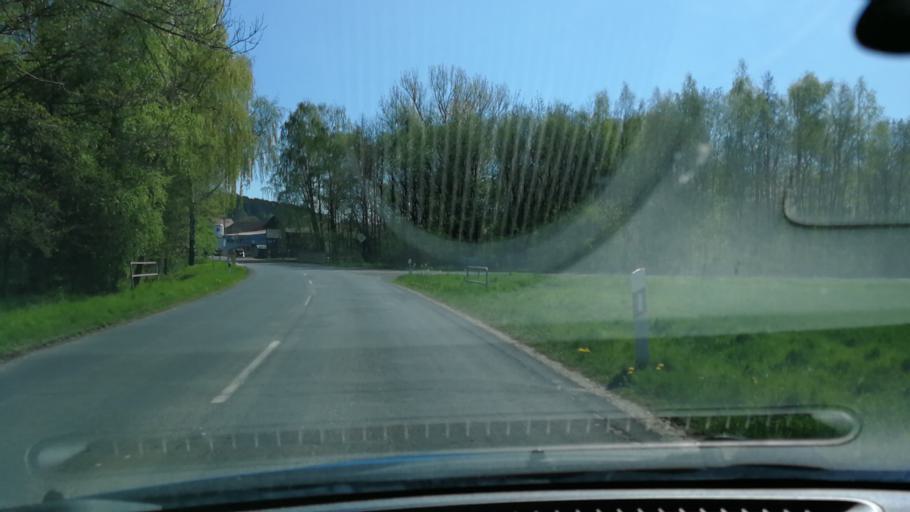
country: DE
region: Lower Saxony
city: Dransfeld
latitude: 51.5194
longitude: 9.7250
